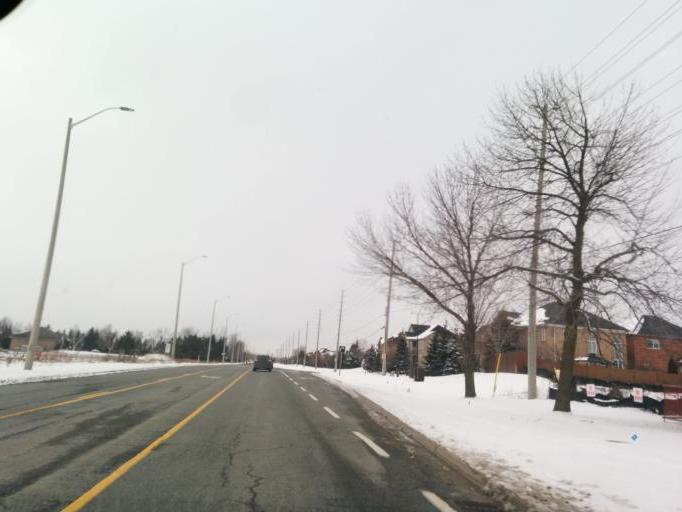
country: CA
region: Ontario
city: Mississauga
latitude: 43.5436
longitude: -79.7447
